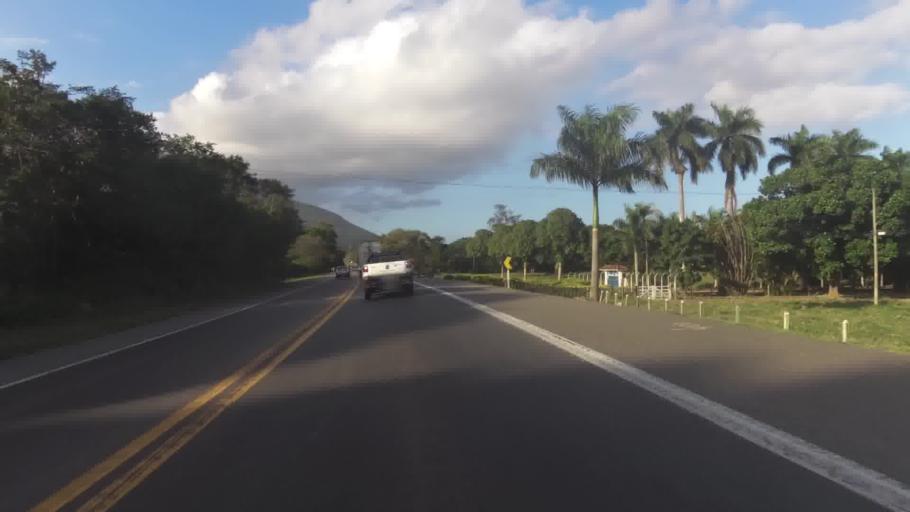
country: BR
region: Espirito Santo
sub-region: Guarapari
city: Guarapari
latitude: -20.6388
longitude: -40.5445
